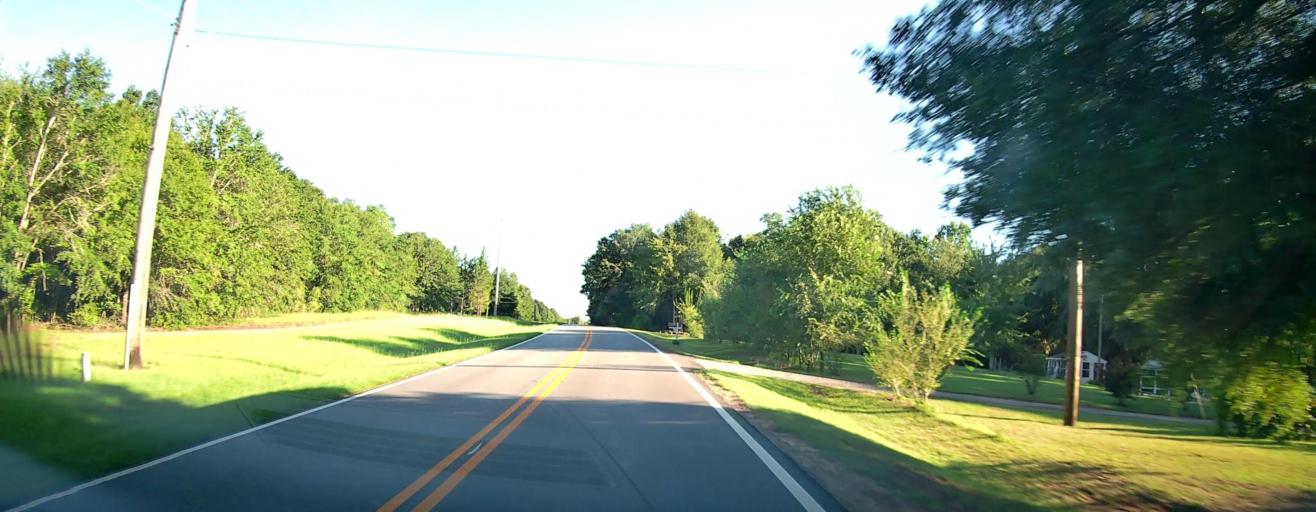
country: US
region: Georgia
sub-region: Pulaski County
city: Hawkinsville
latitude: 32.2958
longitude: -83.4499
